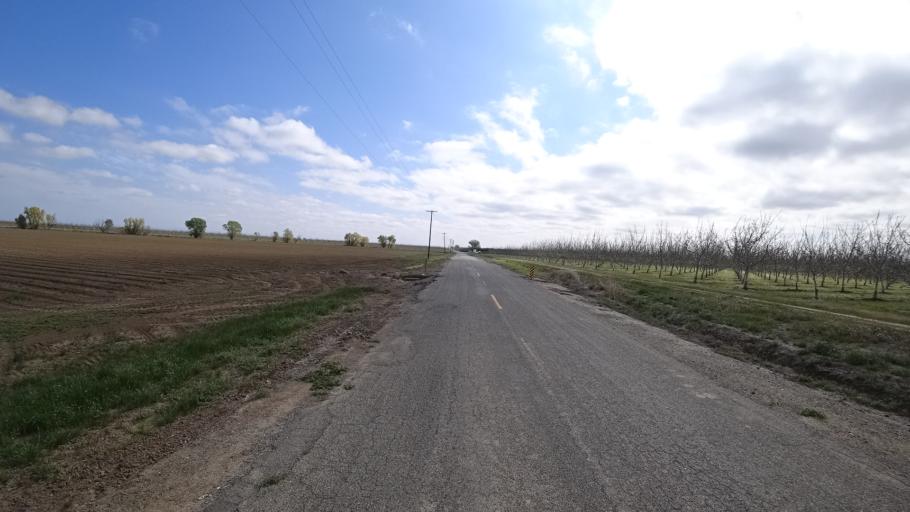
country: US
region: California
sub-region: Colusa County
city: Colusa
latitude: 39.4202
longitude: -121.9518
